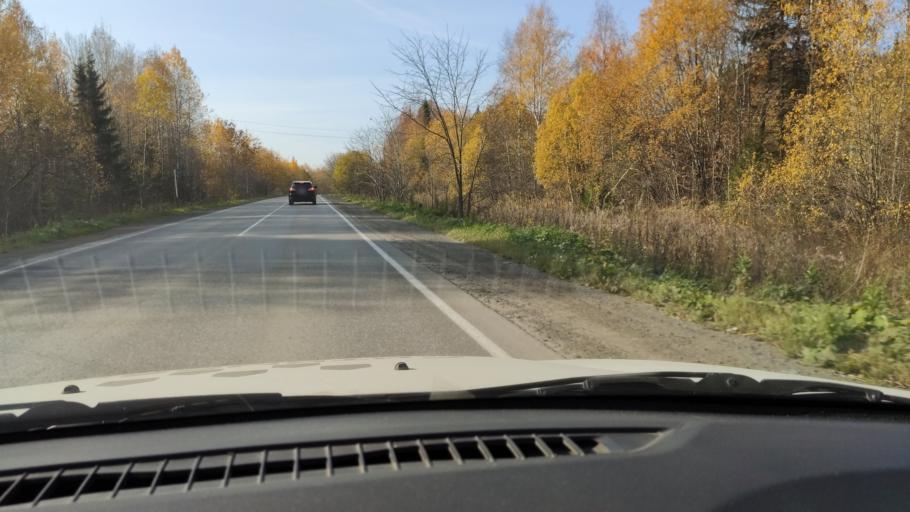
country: RU
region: Perm
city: Novyye Lyady
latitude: 58.0211
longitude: 56.6469
